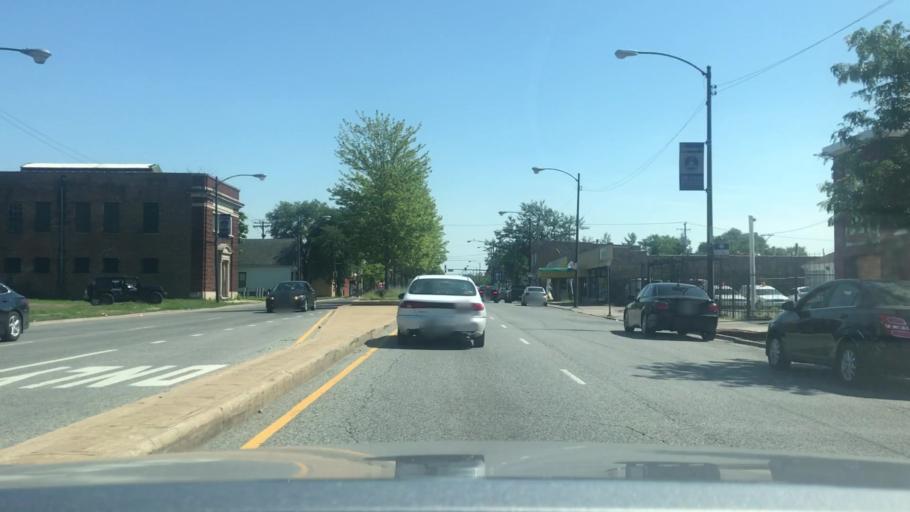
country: US
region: Illinois
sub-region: Cook County
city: Calumet Park
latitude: 41.7086
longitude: -87.6429
